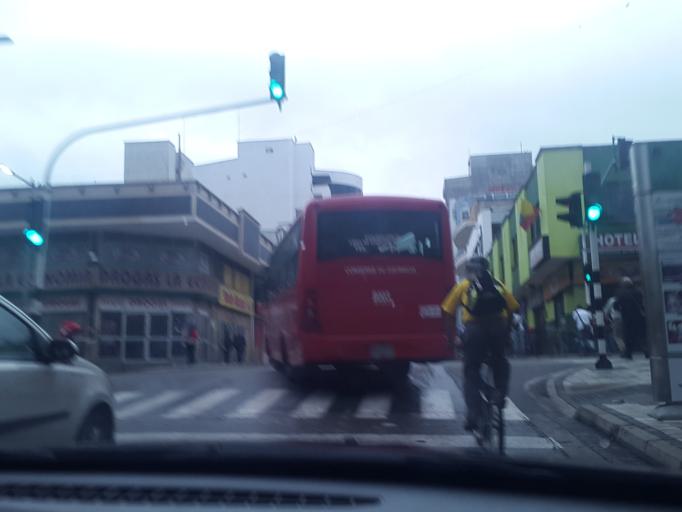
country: CO
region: Quindio
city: Armenia
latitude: 4.5347
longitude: -75.6753
